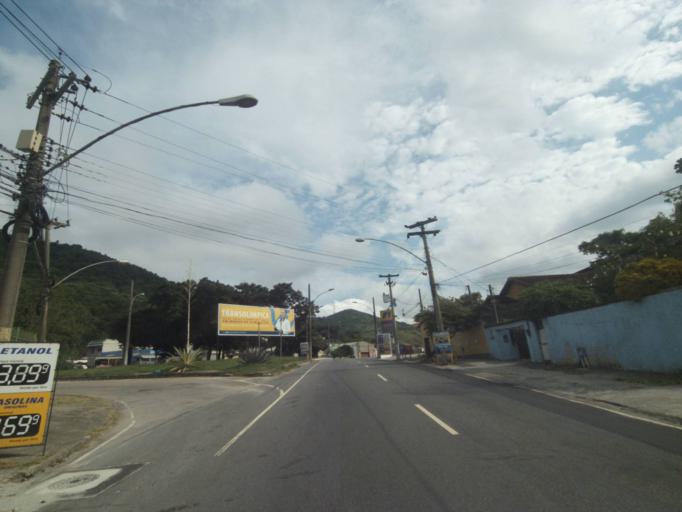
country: BR
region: Rio de Janeiro
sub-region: Nilopolis
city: Nilopolis
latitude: -22.8923
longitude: -43.3948
